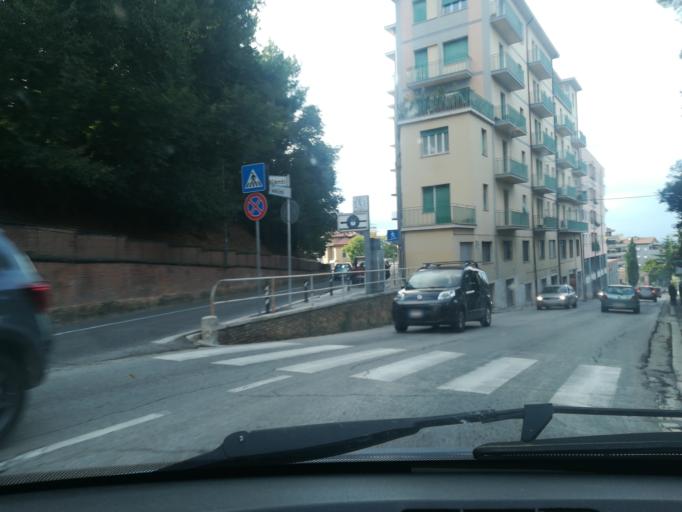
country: IT
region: The Marches
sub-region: Provincia di Macerata
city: Macerata
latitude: 43.3024
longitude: 13.4410
